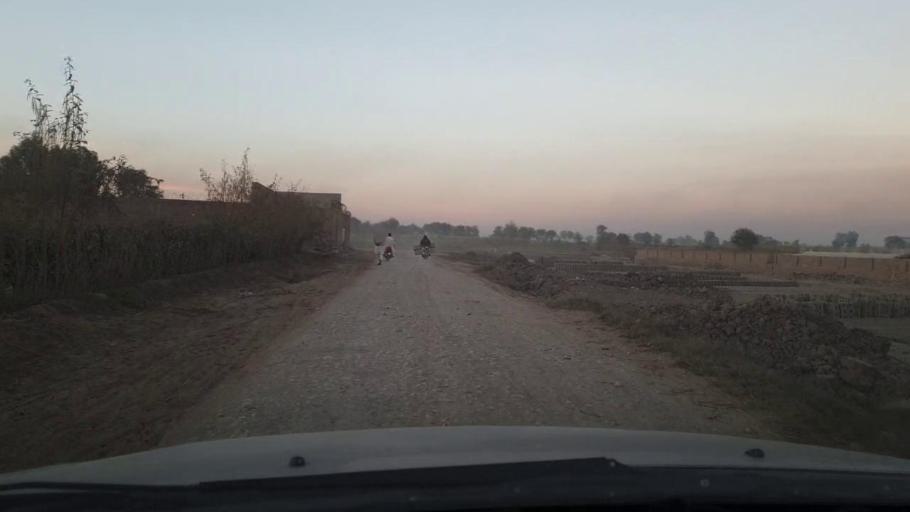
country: PK
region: Sindh
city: Ghotki
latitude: 27.9806
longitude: 69.2840
